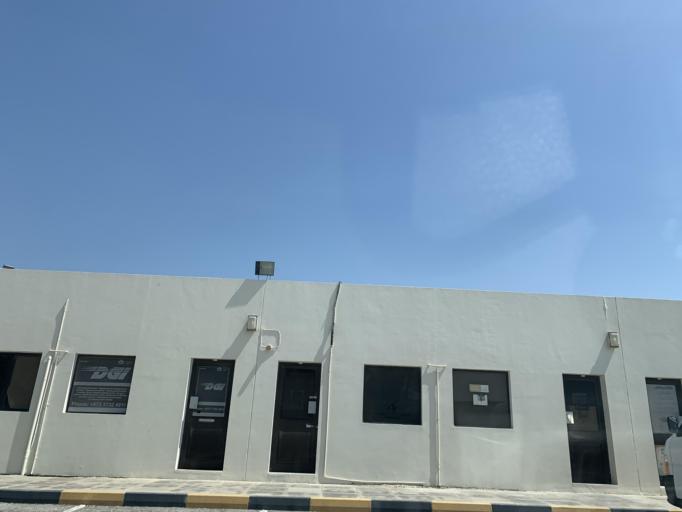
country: BH
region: Muharraq
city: Al Muharraq
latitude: 26.2719
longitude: 50.6194
